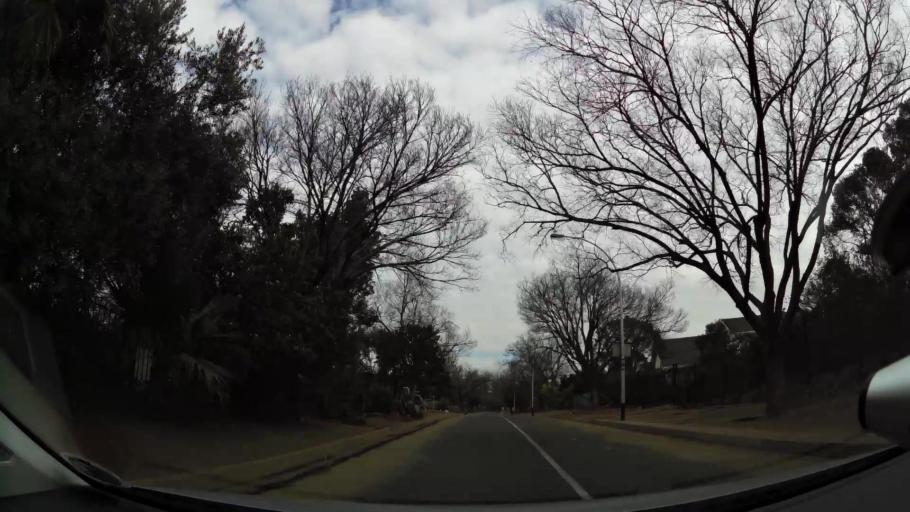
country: ZA
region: Orange Free State
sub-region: Mangaung Metropolitan Municipality
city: Bloemfontein
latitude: -29.0933
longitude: 26.2137
